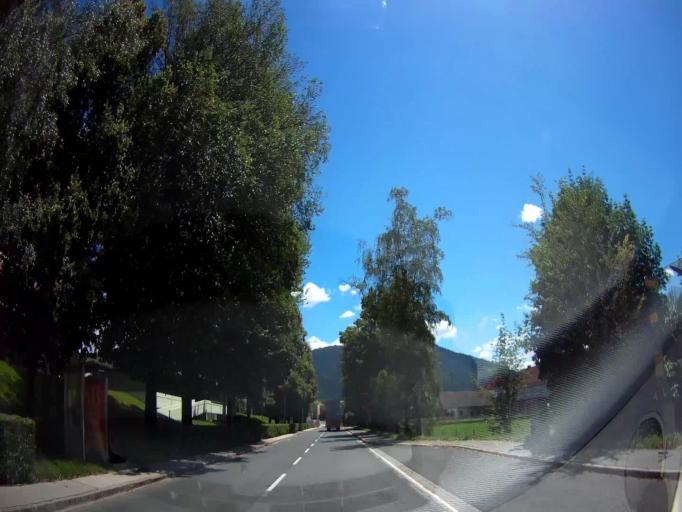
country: AT
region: Carinthia
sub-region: Politischer Bezirk Sankt Veit an der Glan
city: Sankt Veit an der Glan
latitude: 46.7486
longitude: 14.3822
